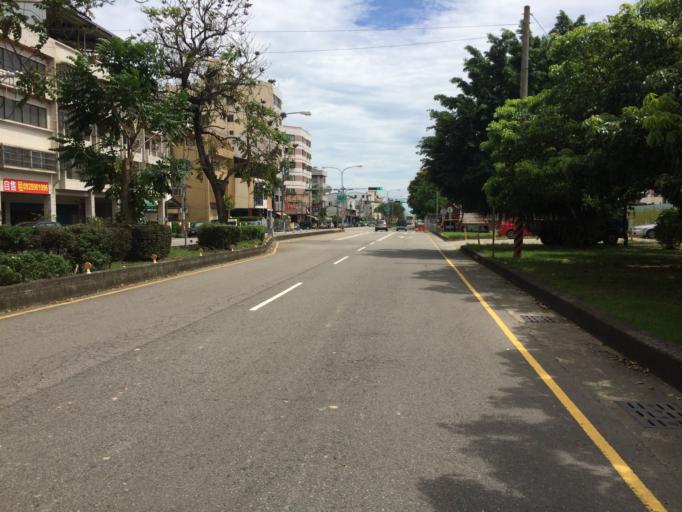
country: TW
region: Taiwan
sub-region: Taichung City
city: Taichung
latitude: 24.1516
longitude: 120.6984
